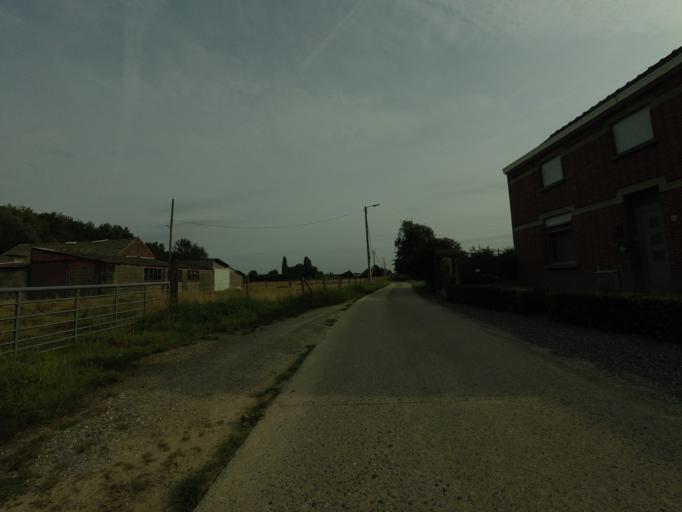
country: BE
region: Flanders
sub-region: Provincie Vlaams-Brabant
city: Kampenhout
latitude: 50.9462
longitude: 4.5365
